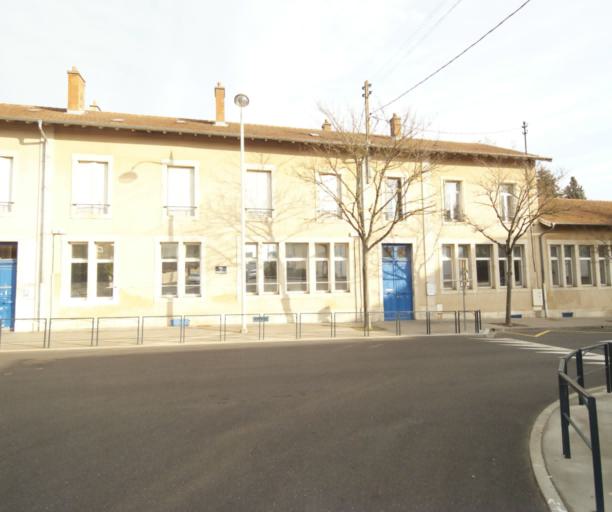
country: FR
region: Lorraine
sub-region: Departement de Meurthe-et-Moselle
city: Maxeville
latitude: 48.6979
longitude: 6.1643
